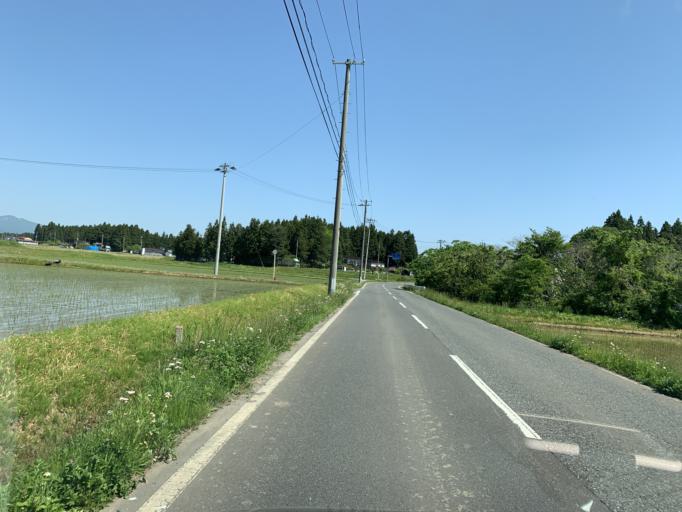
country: JP
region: Iwate
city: Mizusawa
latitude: 39.0679
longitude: 141.0621
